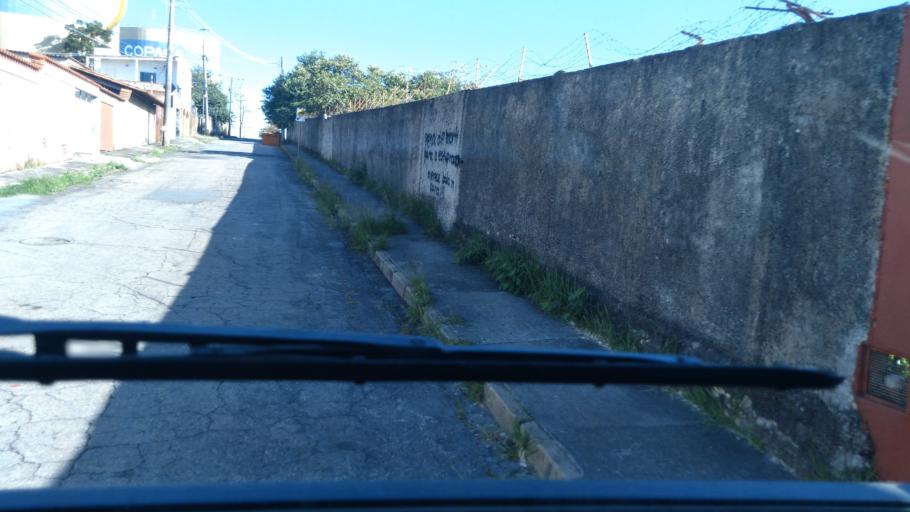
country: BR
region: Minas Gerais
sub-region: Belo Horizonte
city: Belo Horizonte
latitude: -19.8756
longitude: -43.9103
